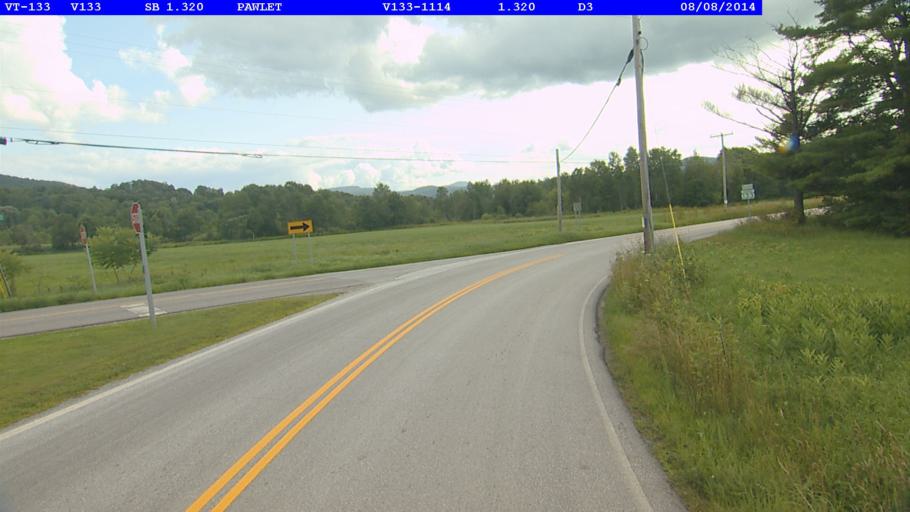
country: US
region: New York
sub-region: Washington County
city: Granville
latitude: 43.3518
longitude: -73.1530
